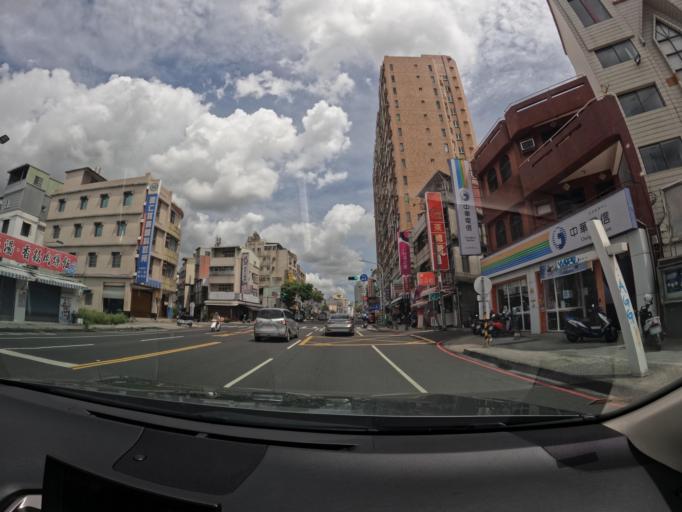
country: TW
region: Kaohsiung
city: Kaohsiung
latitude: 22.7123
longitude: 120.2918
